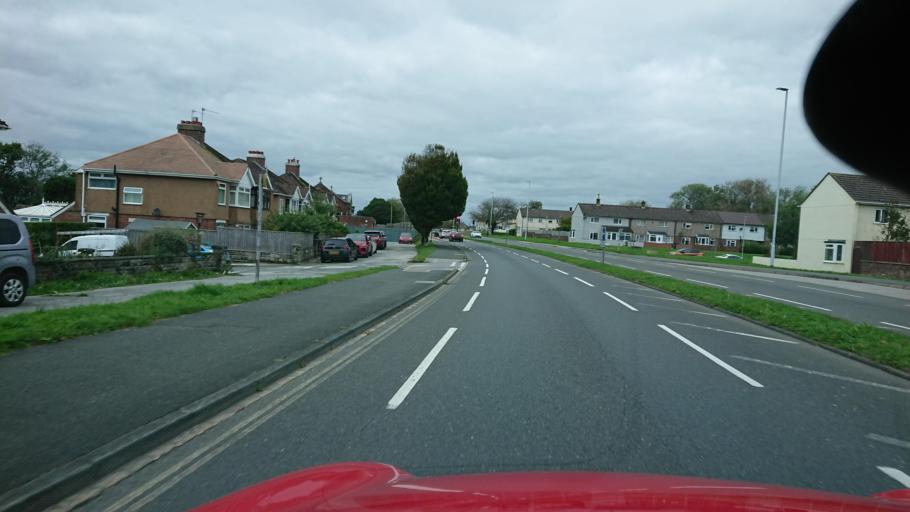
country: GB
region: England
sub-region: Plymouth
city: Plymouth
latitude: 50.4111
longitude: -4.1394
